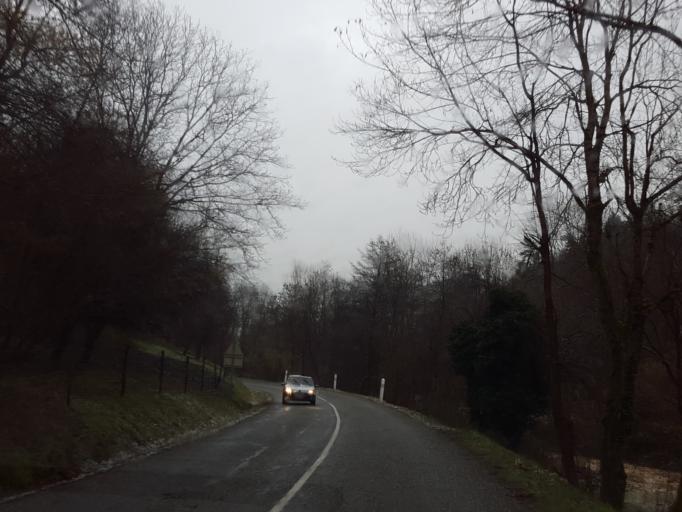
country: FR
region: Midi-Pyrenees
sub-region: Departement de l'Ariege
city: Saint-Girons
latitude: 42.9002
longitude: 1.3036
